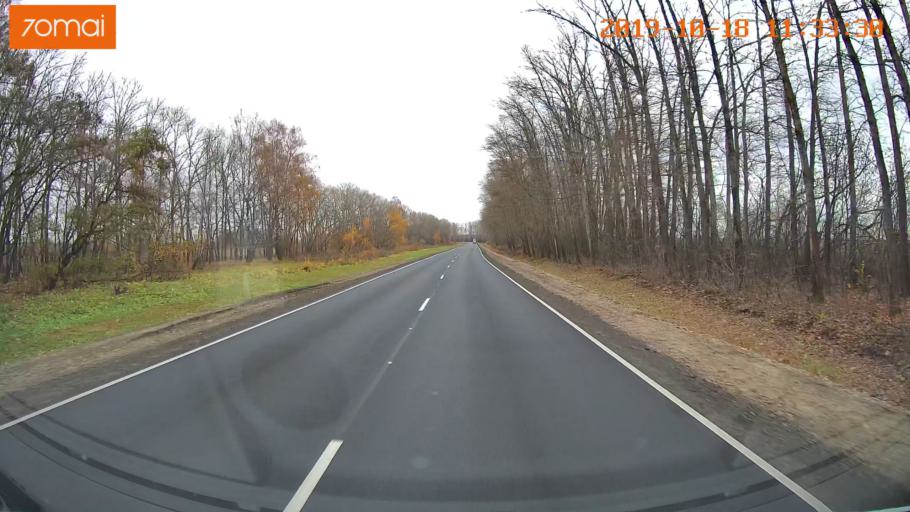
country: RU
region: Rjazan
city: Oktyabr'skiy
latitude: 54.1407
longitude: 38.7420
